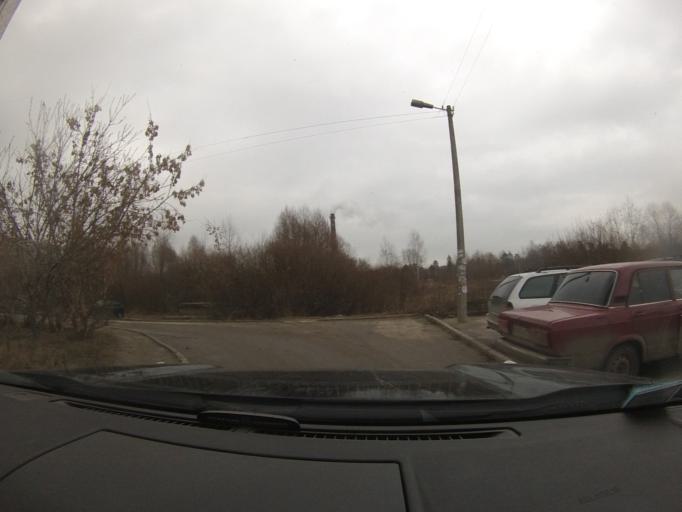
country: RU
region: Moskovskaya
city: Peski
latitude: 55.2727
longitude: 38.7551
